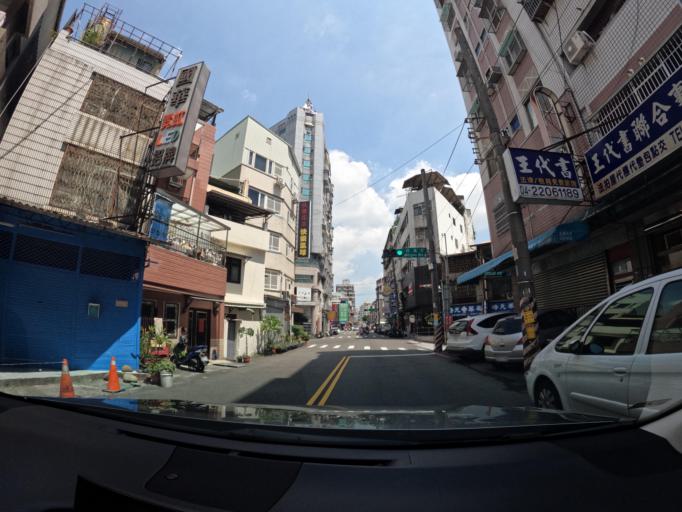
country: TW
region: Taiwan
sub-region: Taichung City
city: Taichung
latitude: 24.1518
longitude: 120.6717
